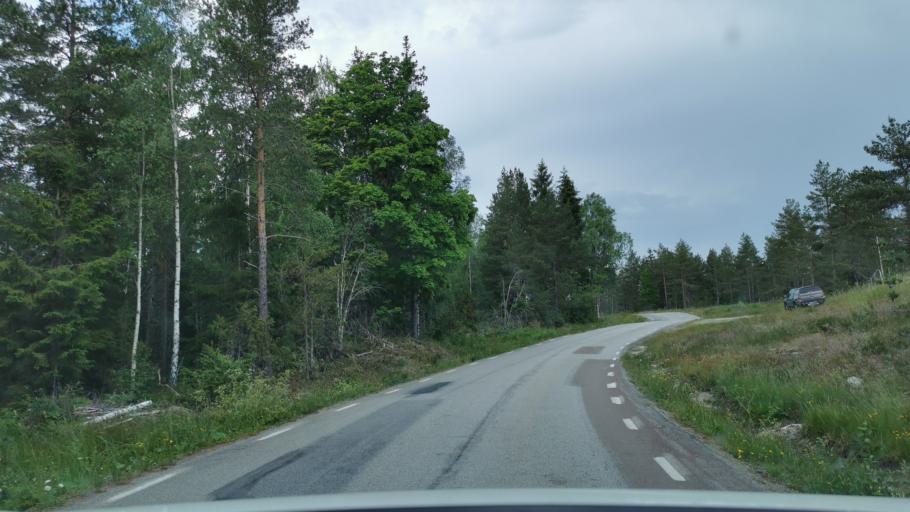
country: SE
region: Vaestra Goetaland
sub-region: Bengtsfors Kommun
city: Dals Langed
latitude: 58.8782
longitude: 12.4043
